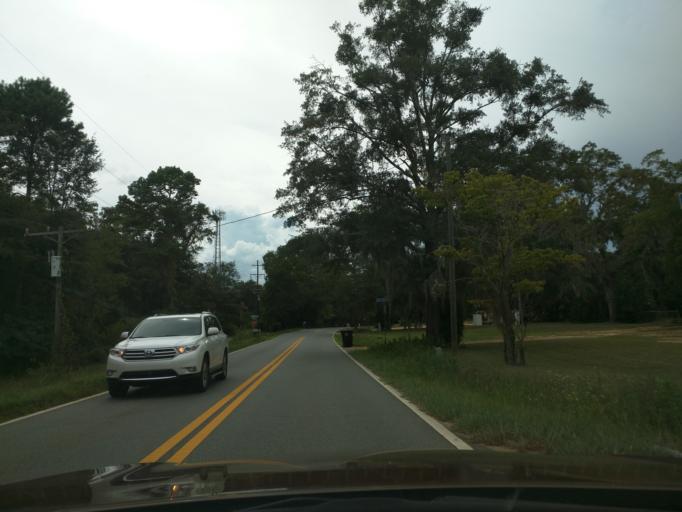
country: US
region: Florida
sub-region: Gadsden County
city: Havana
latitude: 30.5872
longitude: -84.2715
